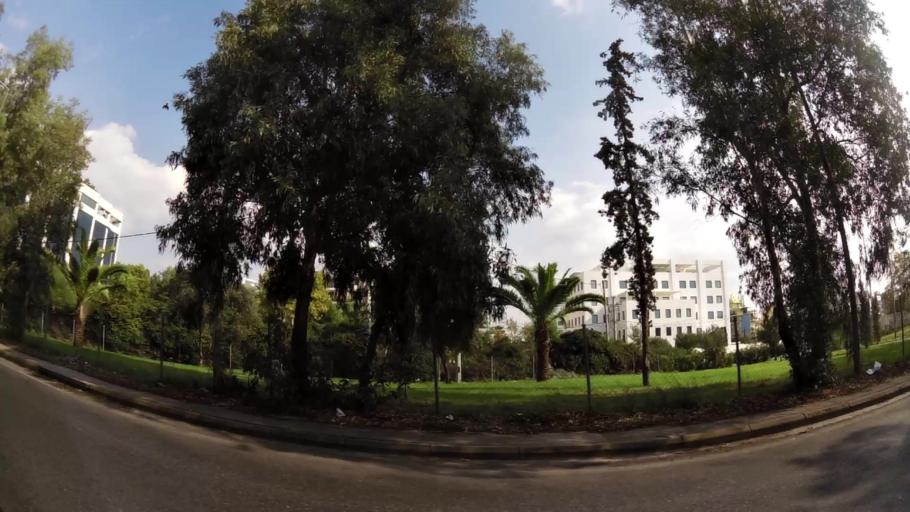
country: GR
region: Attica
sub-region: Nomarchia Athinas
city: Kallithea
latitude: 37.9390
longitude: 23.6948
